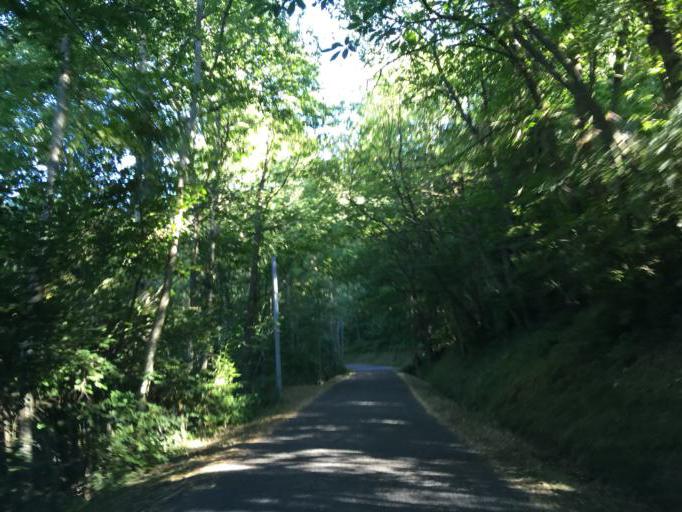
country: FR
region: Rhone-Alpes
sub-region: Departement de la Loire
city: Saint-Jean-Bonnefonds
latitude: 45.4319
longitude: 4.4737
